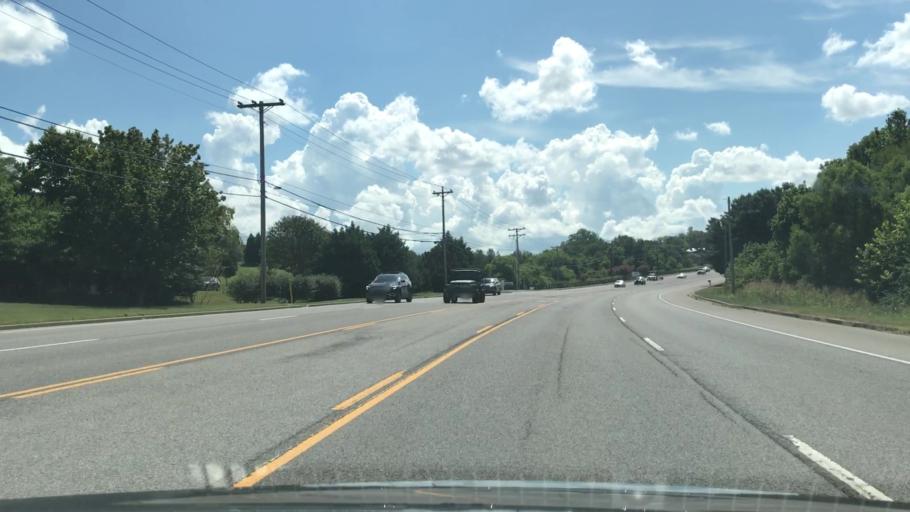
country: US
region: Tennessee
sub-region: Williamson County
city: Franklin
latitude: 35.9086
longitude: -86.8071
